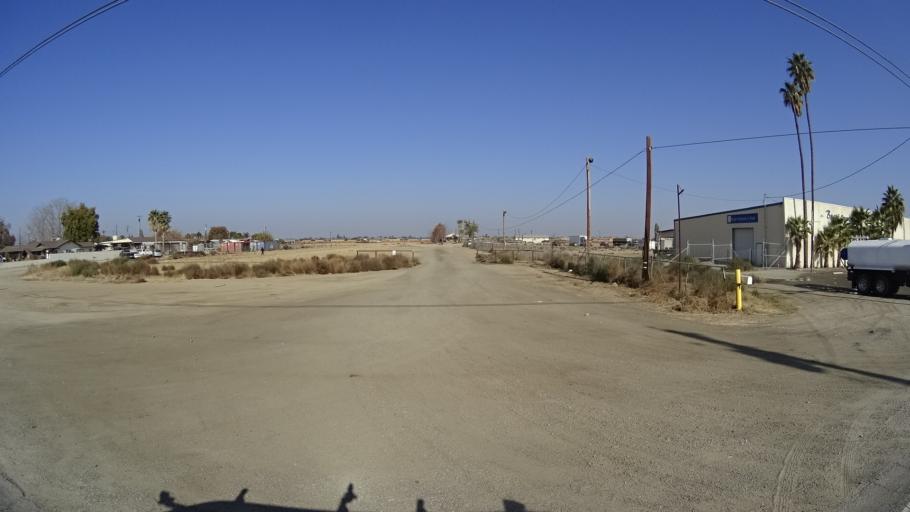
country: US
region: California
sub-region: Kern County
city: Greenfield
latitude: 35.2668
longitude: -119.0322
